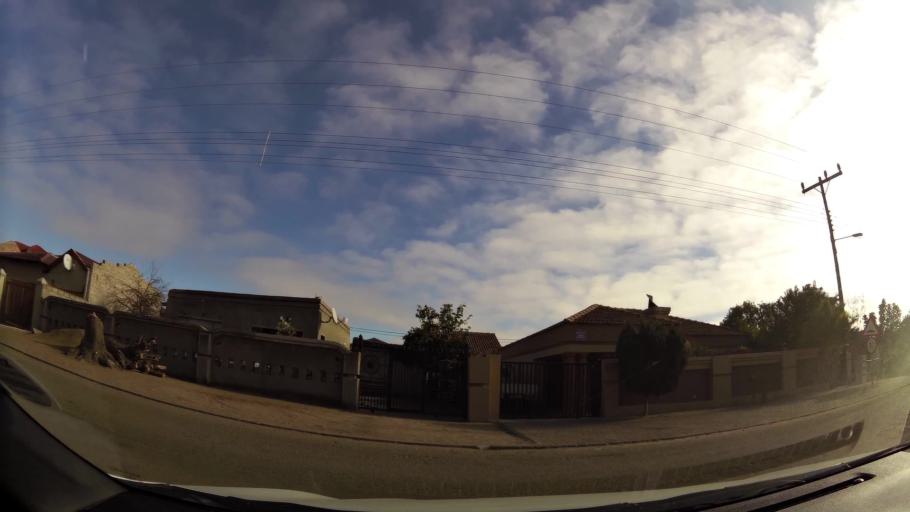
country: ZA
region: Limpopo
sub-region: Capricorn District Municipality
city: Polokwane
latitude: -23.8453
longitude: 29.3868
